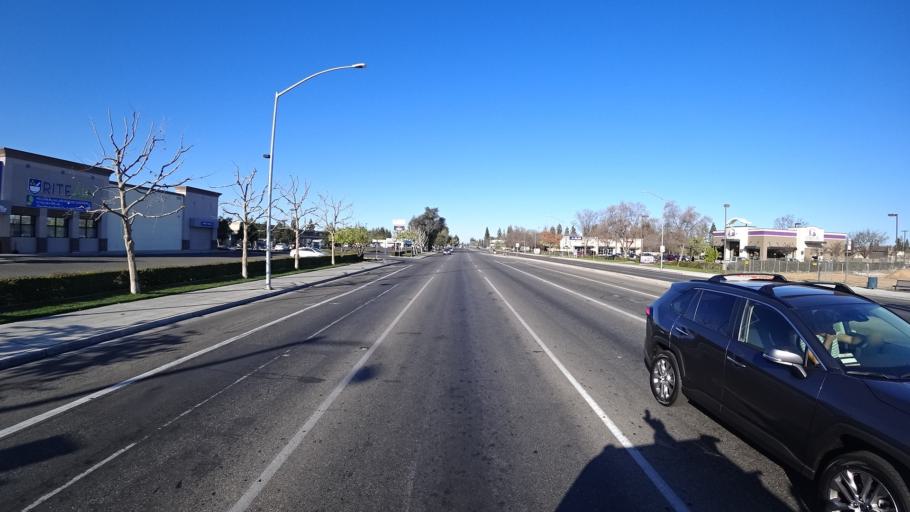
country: US
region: California
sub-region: Fresno County
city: Fresno
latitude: 36.8082
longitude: -119.8267
